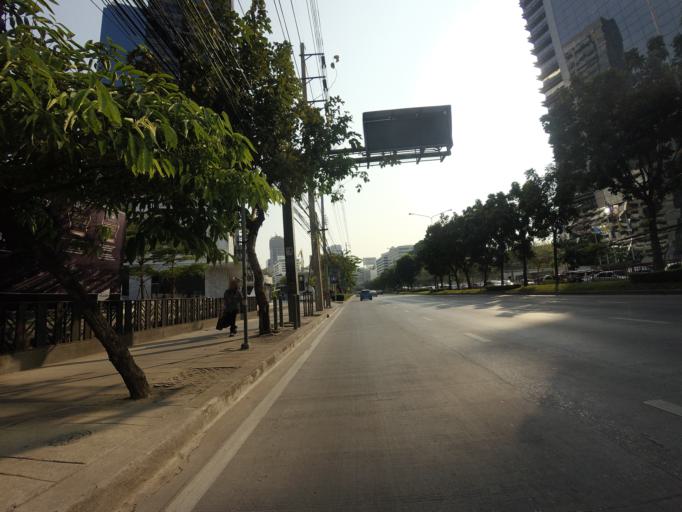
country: TH
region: Bangkok
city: Din Daeng
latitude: 13.7637
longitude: 100.5685
